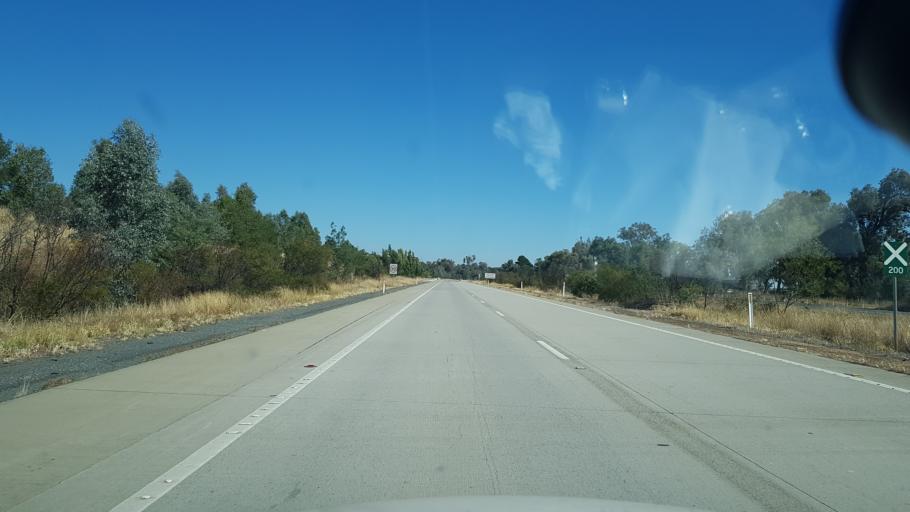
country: AU
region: New South Wales
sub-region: Greater Hume Shire
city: Holbrook
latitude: -35.8975
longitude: 147.1671
